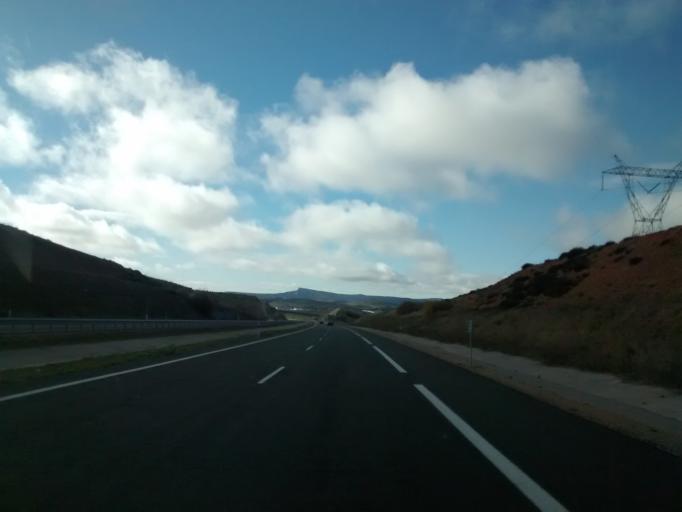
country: ES
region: Castille and Leon
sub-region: Provincia de Palencia
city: Aguilar de Campoo
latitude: 42.8064
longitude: -4.2285
